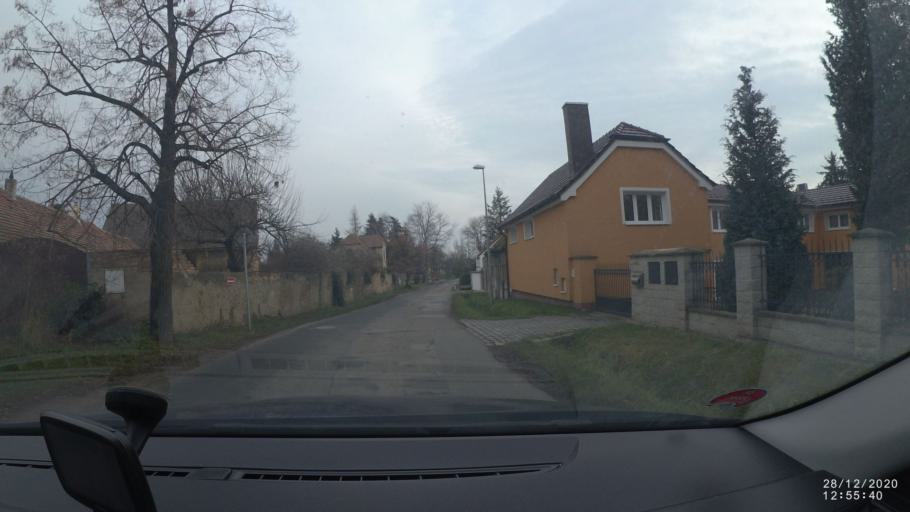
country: CZ
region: Praha
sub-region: Praha 19
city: Satalice
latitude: 50.1552
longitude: 14.5797
